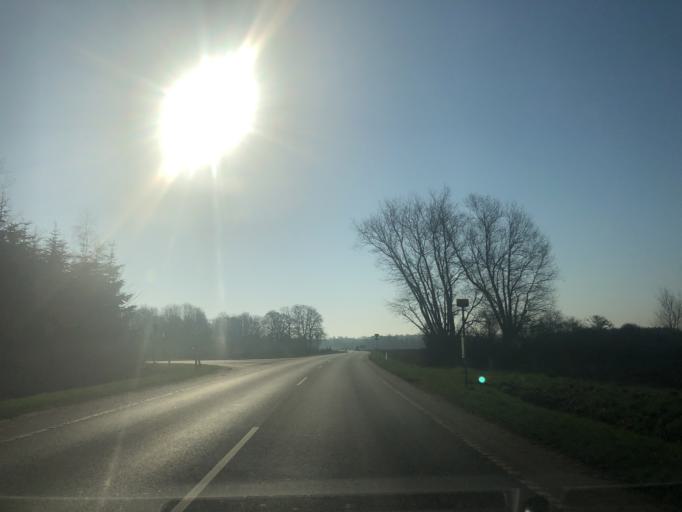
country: DK
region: Zealand
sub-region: Faxe Kommune
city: Ronnede
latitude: 55.2875
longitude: 12.0310
